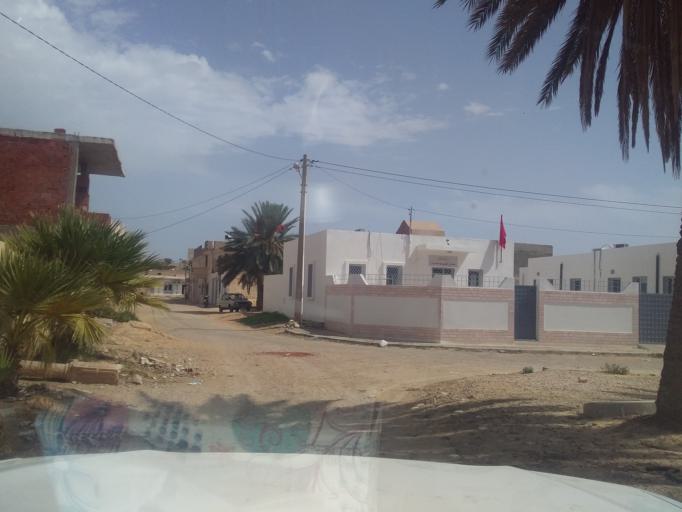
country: TN
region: Madanin
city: Medenine
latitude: 33.5846
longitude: 10.3197
